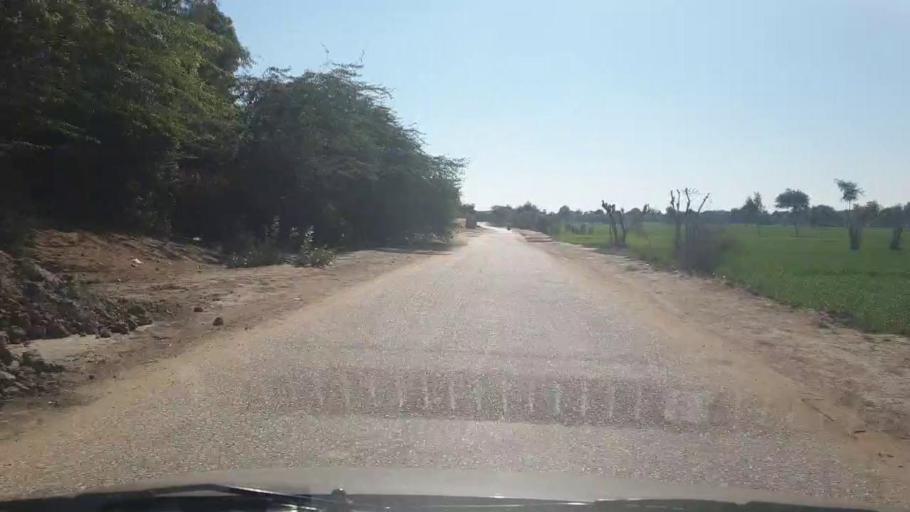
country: PK
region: Sindh
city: Bozdar
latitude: 27.0549
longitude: 68.6479
